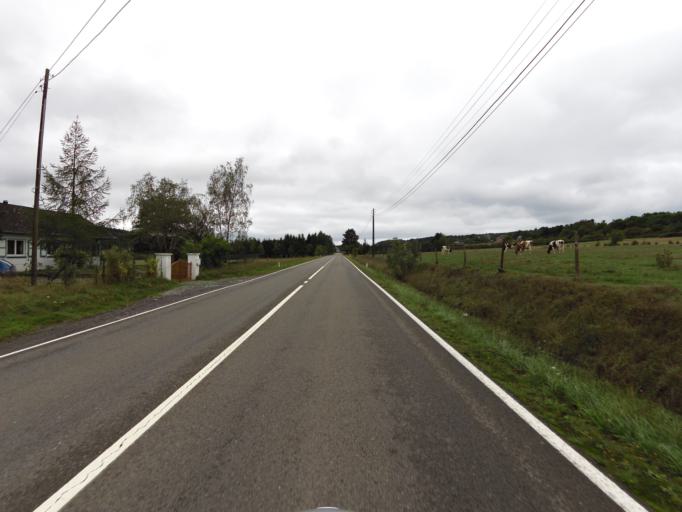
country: BE
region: Wallonia
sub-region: Province du Luxembourg
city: Wellin
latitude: 50.1102
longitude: 5.1553
